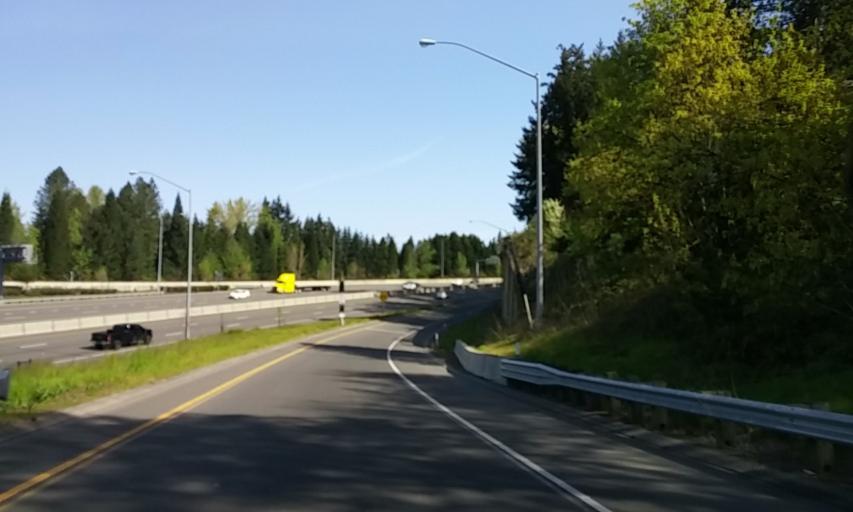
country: US
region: Oregon
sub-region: Washington County
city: Cedar Hills
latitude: 45.4990
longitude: -122.7896
